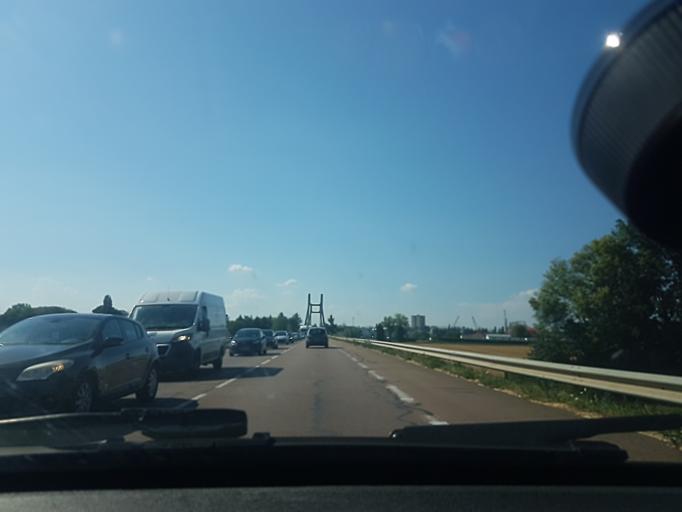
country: FR
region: Bourgogne
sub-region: Departement de Saone-et-Loire
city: Saint-Marcel
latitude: 46.7812
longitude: 4.8750
